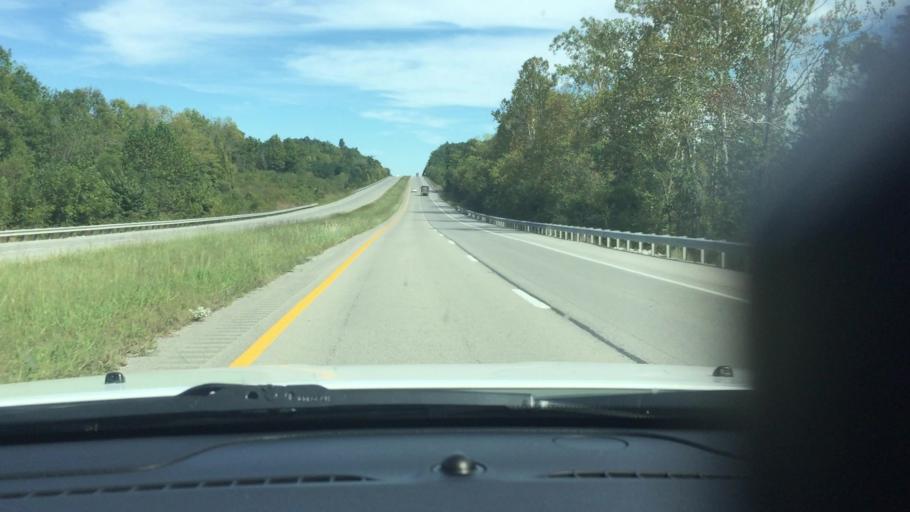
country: US
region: Kentucky
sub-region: Caldwell County
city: Princeton
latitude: 37.1395
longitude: -87.8466
